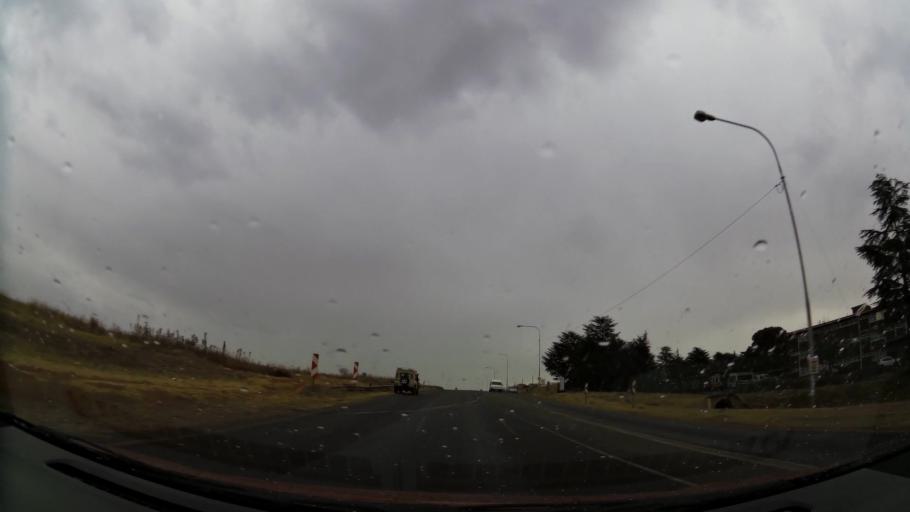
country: ZA
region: Gauteng
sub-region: City of Johannesburg Metropolitan Municipality
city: Roodepoort
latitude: -26.1742
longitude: 27.8047
